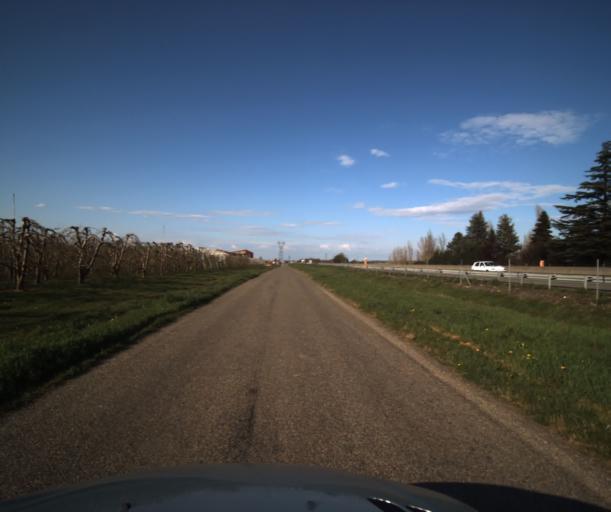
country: FR
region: Midi-Pyrenees
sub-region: Departement du Tarn-et-Garonne
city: Bressols
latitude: 43.9512
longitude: 1.3249
